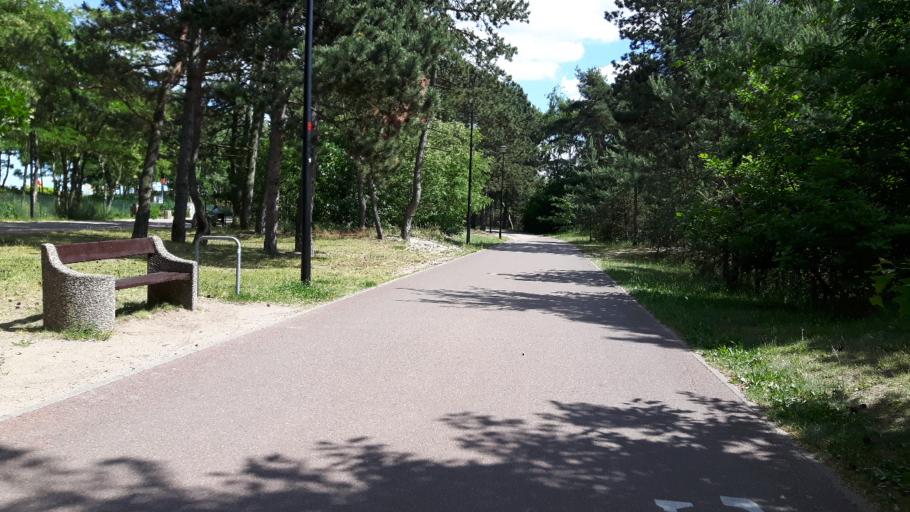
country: PL
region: Pomeranian Voivodeship
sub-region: Gdansk
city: Gdansk
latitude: 54.4124
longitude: 18.6257
